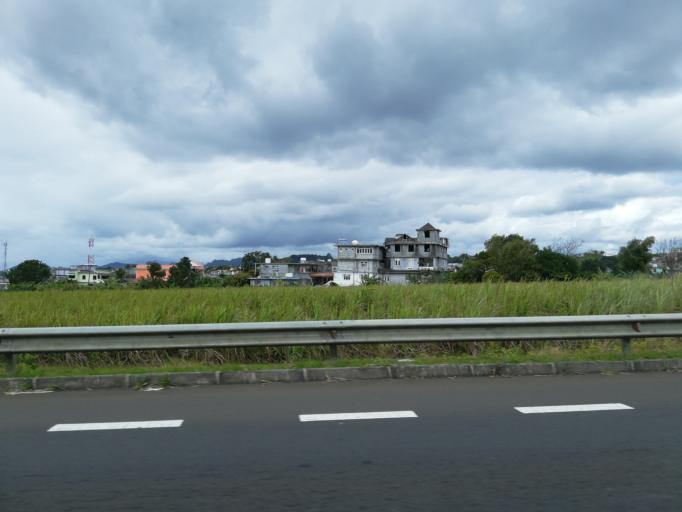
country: MU
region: Moka
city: Quartier Militaire
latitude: -20.2420
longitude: 57.5971
